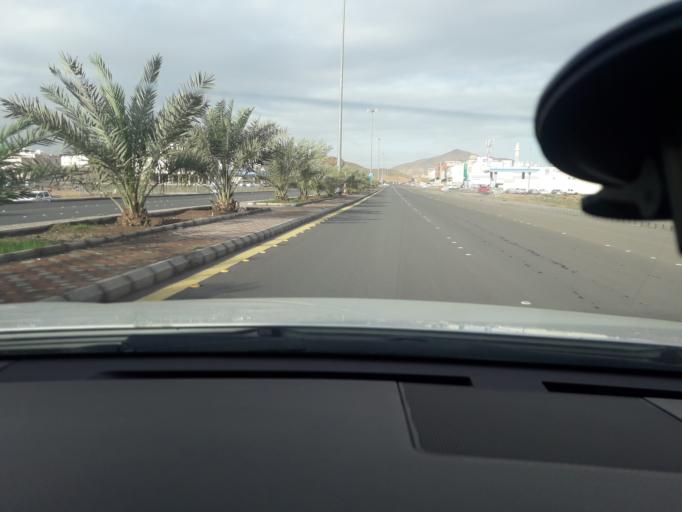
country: SA
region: Al Madinah al Munawwarah
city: Sultanah
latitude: 24.4652
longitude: 39.5109
